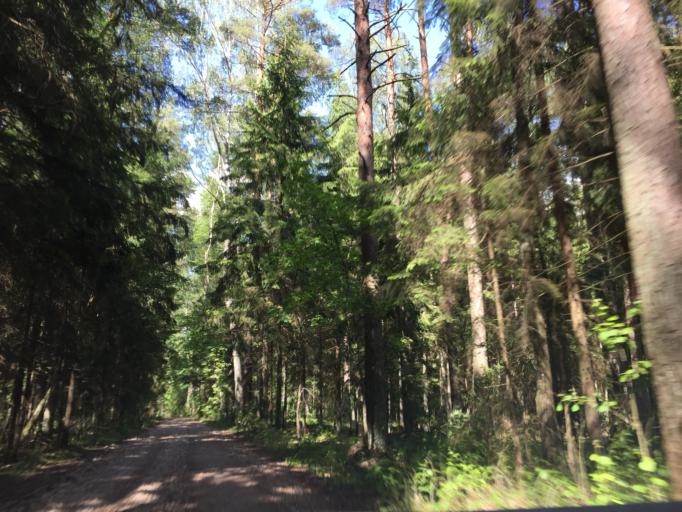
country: LV
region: Engure
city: Smarde
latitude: 56.8194
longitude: 23.3903
